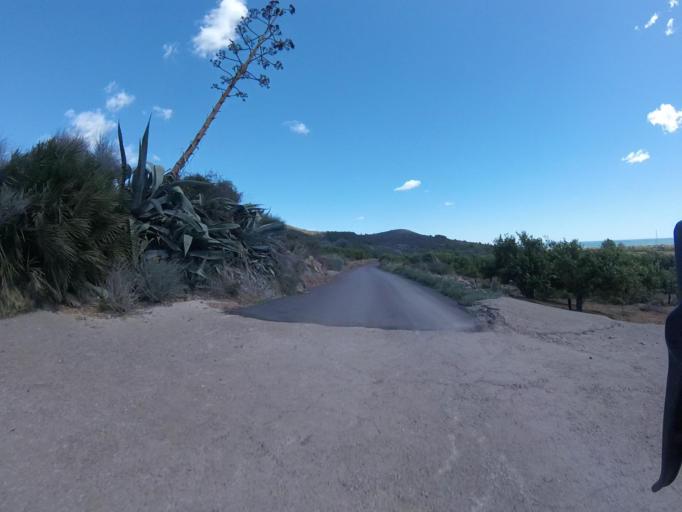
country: ES
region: Valencia
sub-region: Provincia de Castello
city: Orpesa/Oropesa del Mar
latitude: 40.1681
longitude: 0.1432
